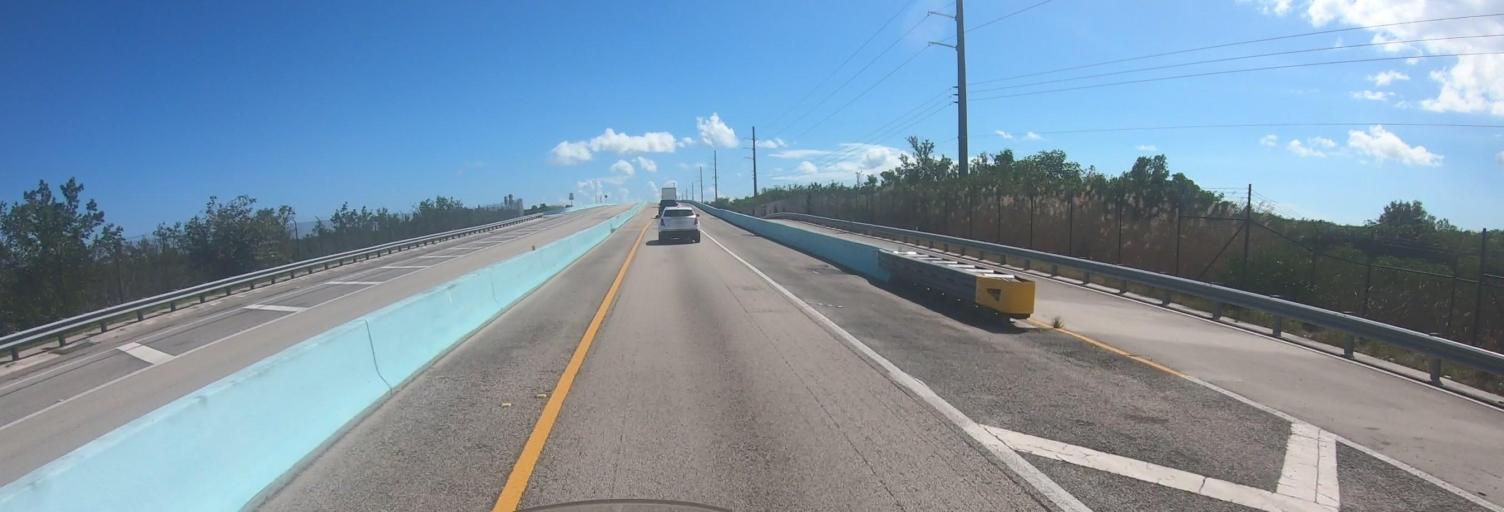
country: US
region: Florida
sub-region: Monroe County
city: North Key Largo
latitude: 25.2927
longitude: -80.4456
